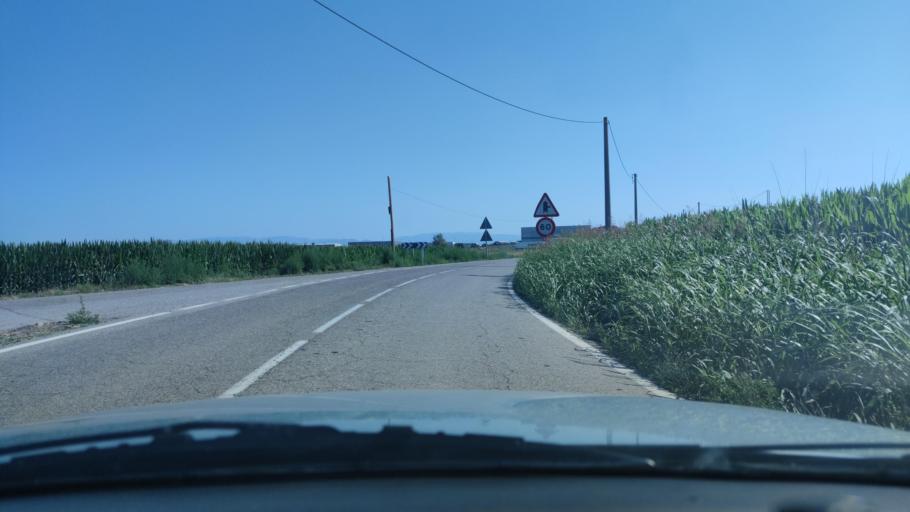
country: ES
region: Catalonia
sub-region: Provincia de Lleida
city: Sidamon
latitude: 41.6343
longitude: 0.7876
